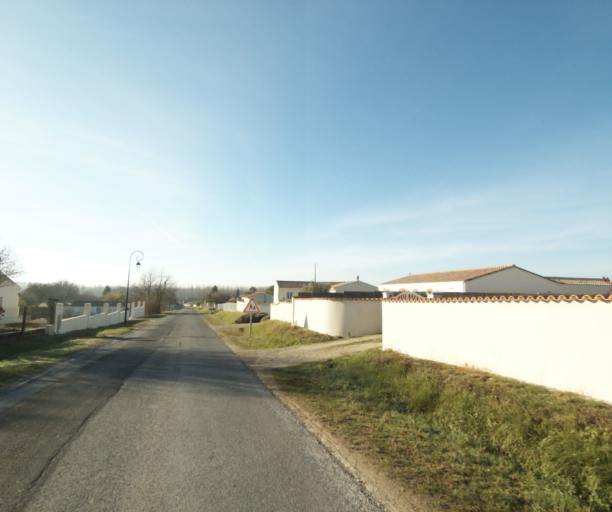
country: FR
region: Poitou-Charentes
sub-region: Departement de la Charente-Maritime
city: Cherac
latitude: 45.6896
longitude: -0.4505
